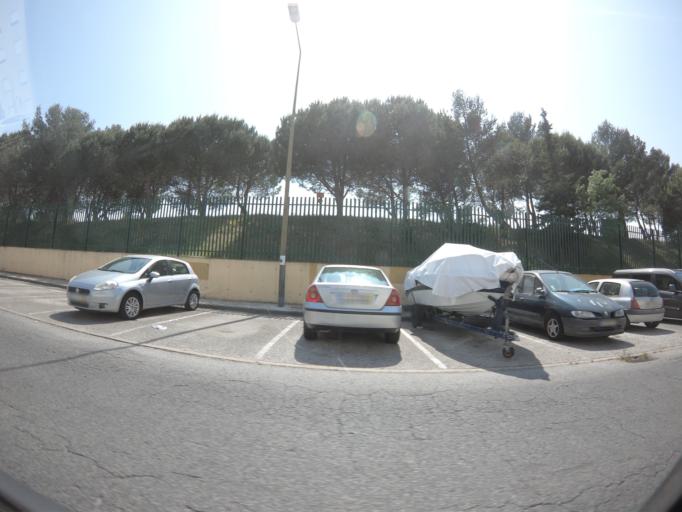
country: PT
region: Lisbon
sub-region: Loures
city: Moscavide
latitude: 38.7522
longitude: -9.1260
